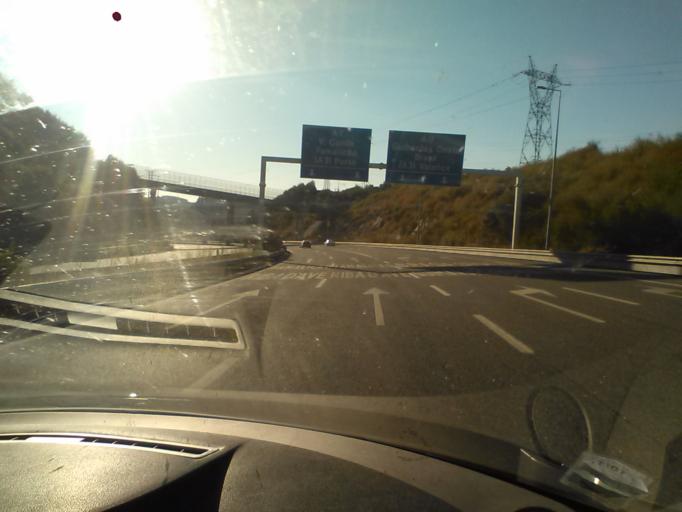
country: PT
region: Braga
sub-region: Guimaraes
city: Candoso
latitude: 41.4282
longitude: -8.3316
